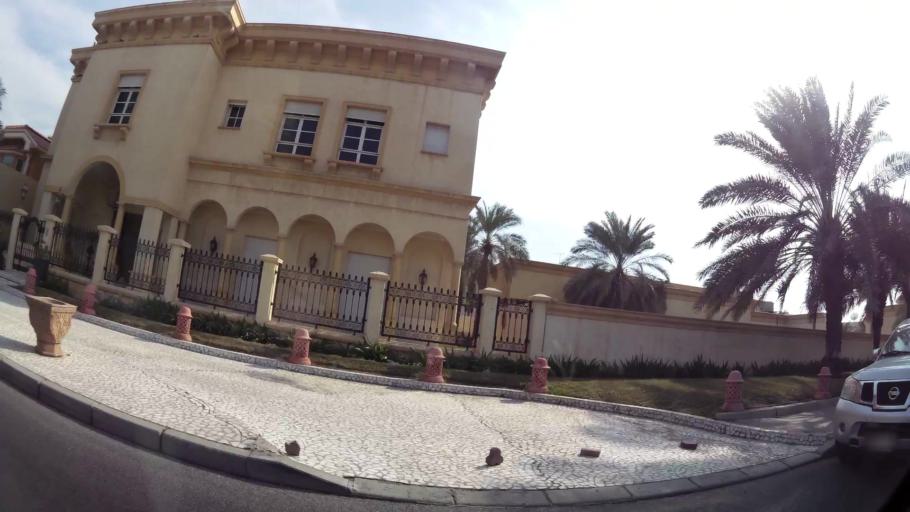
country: KW
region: Al Farwaniyah
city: Al Farwaniyah
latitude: 29.3103
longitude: 47.9732
